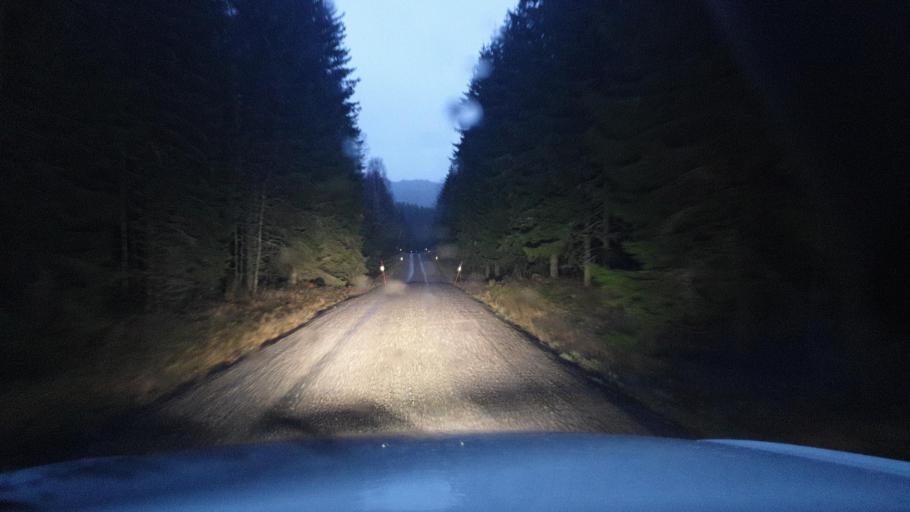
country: SE
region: Vaermland
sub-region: Eda Kommun
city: Charlottenberg
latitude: 60.0288
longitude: 12.6343
